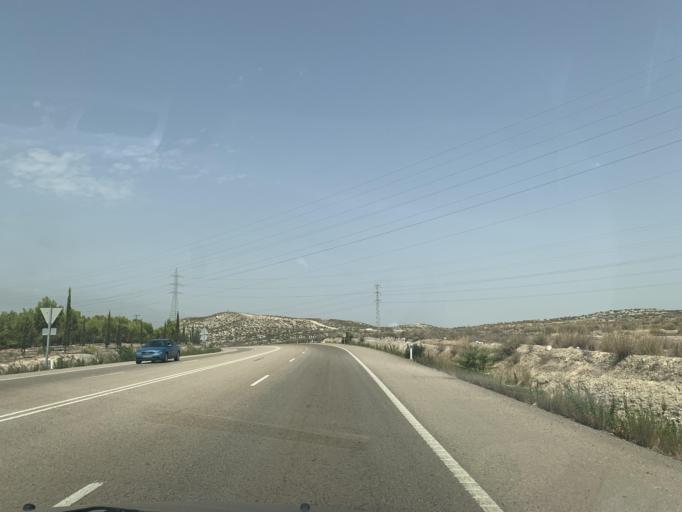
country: ES
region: Aragon
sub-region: Provincia de Zaragoza
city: Zaragoza
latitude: 41.5908
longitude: -0.8317
